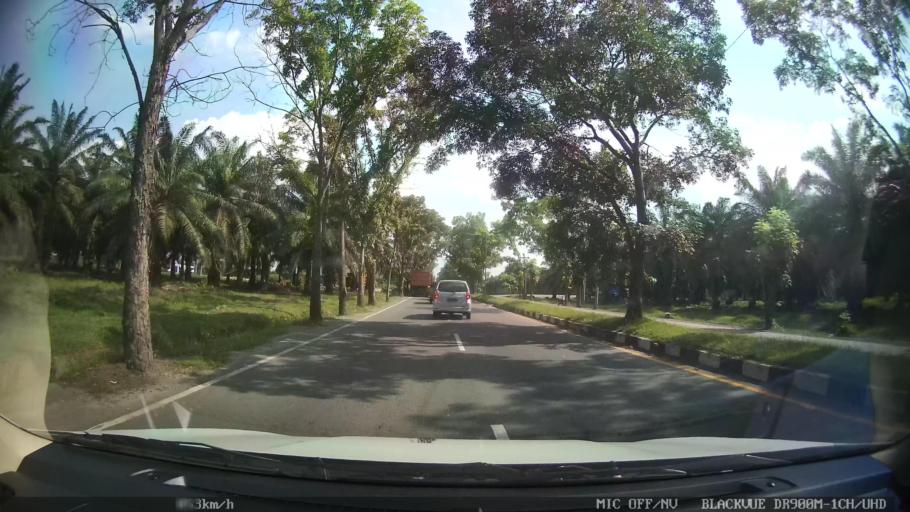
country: ID
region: North Sumatra
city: Binjai
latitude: 3.6366
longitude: 98.5353
